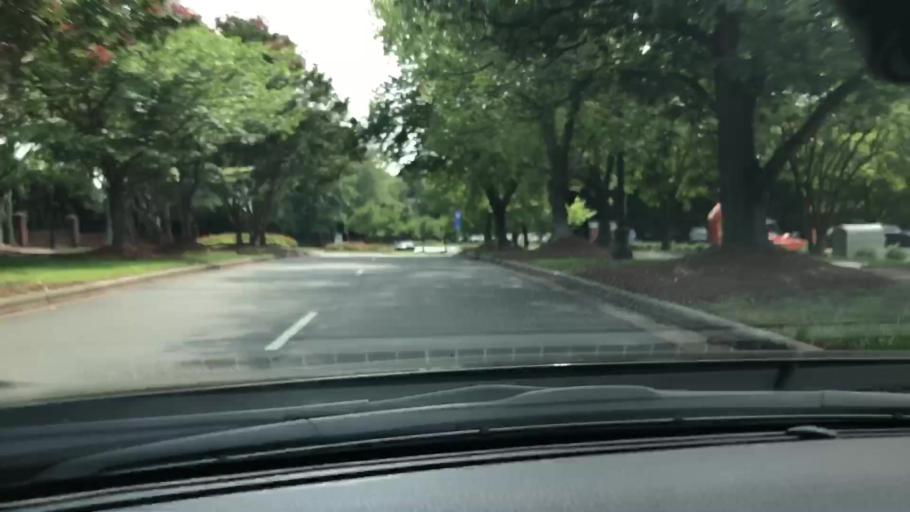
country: US
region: North Carolina
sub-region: Mecklenburg County
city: Charlotte
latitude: 35.1514
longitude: -80.8225
